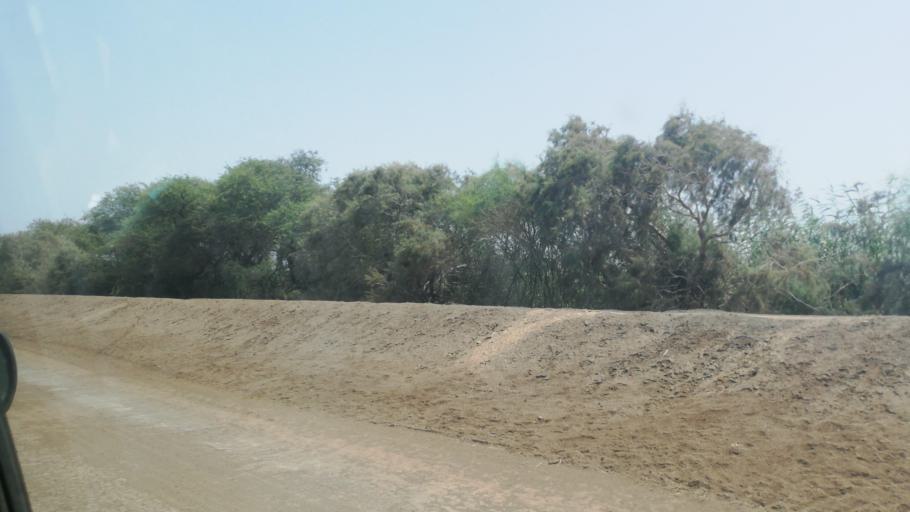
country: SN
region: Saint-Louis
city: Saint-Louis
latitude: 16.4071
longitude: -16.2983
